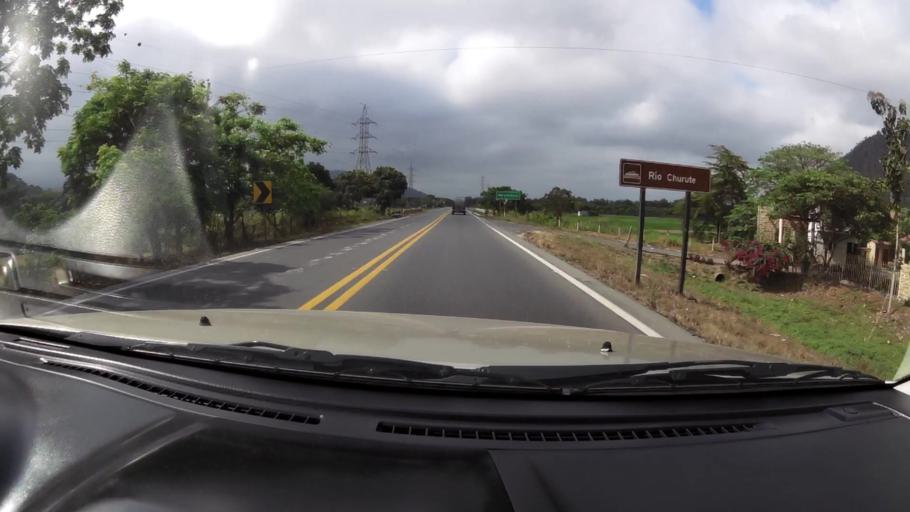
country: EC
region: Guayas
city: Naranjal
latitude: -2.4104
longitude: -79.6235
